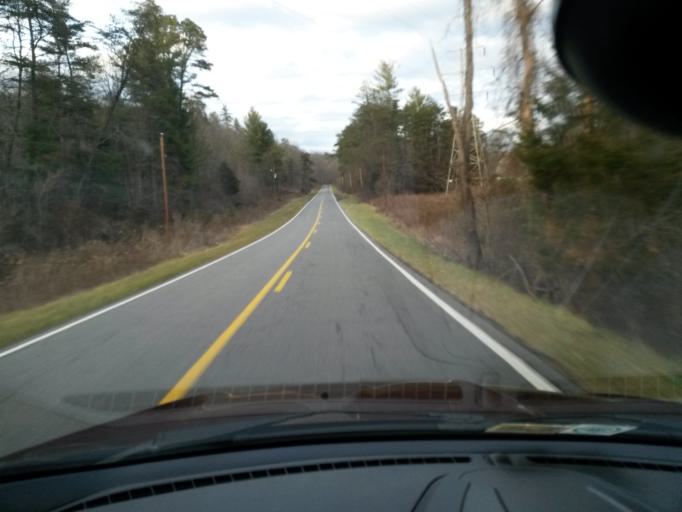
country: US
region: Virginia
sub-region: City of Covington
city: Covington
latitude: 37.7762
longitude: -80.1091
